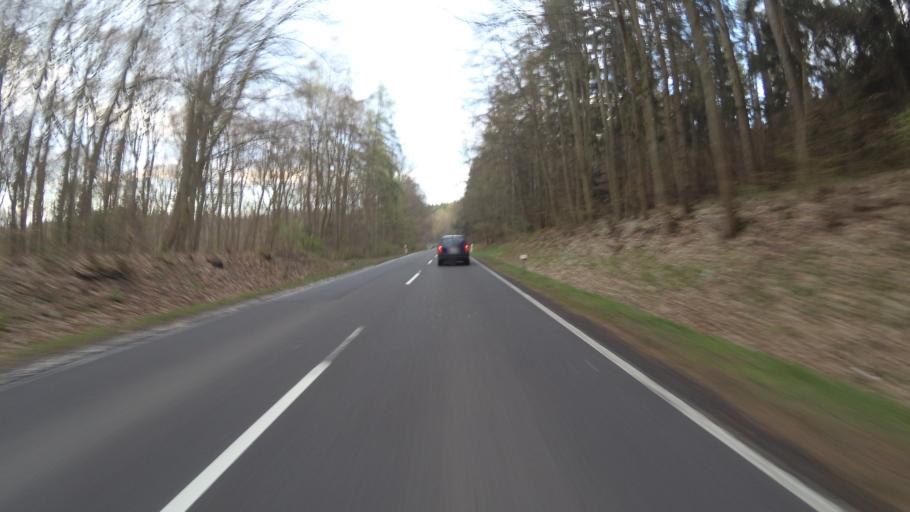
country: DE
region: Rheinland-Pfalz
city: Monzelfeld
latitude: 49.8927
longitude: 7.0441
